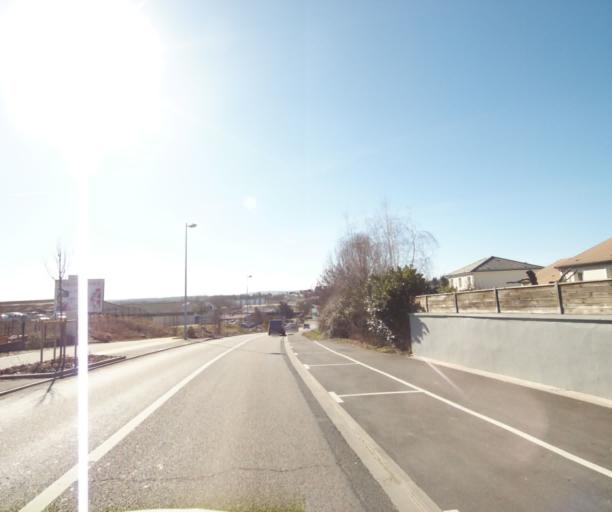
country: FR
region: Lorraine
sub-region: Departement de Meurthe-et-Moselle
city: Ludres
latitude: 48.6207
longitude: 6.1780
